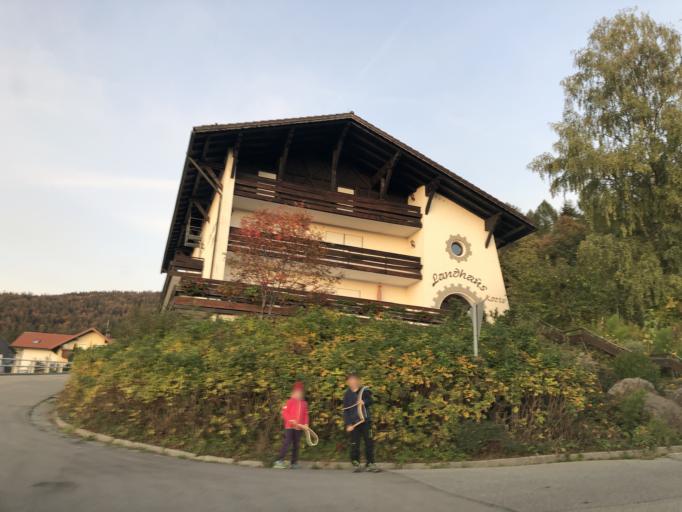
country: DE
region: Bavaria
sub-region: Lower Bavaria
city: Bodenmais
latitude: 49.0729
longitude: 13.1082
